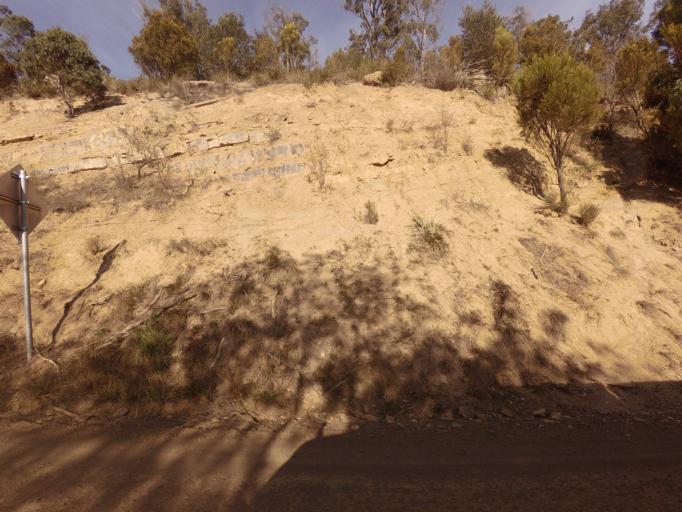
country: AU
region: Tasmania
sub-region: Sorell
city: Sorell
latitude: -42.5010
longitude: 147.4324
